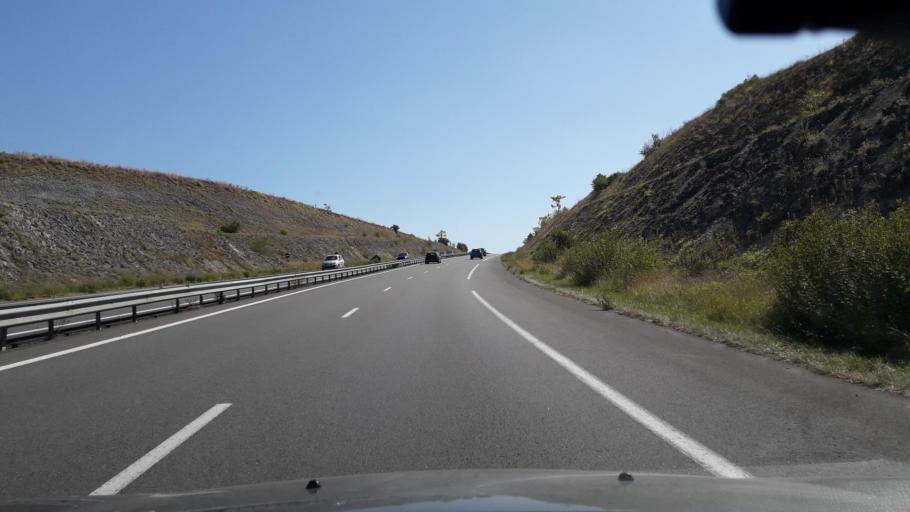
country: FR
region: Poitou-Charentes
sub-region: Departement de la Charente
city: Chassors
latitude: 45.6686
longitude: -0.2101
